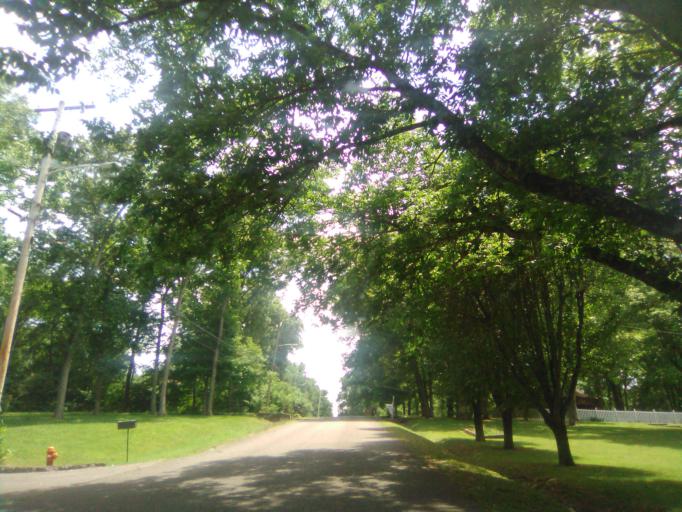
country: US
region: Tennessee
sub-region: Davidson County
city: Belle Meade
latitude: 36.1313
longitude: -86.8809
